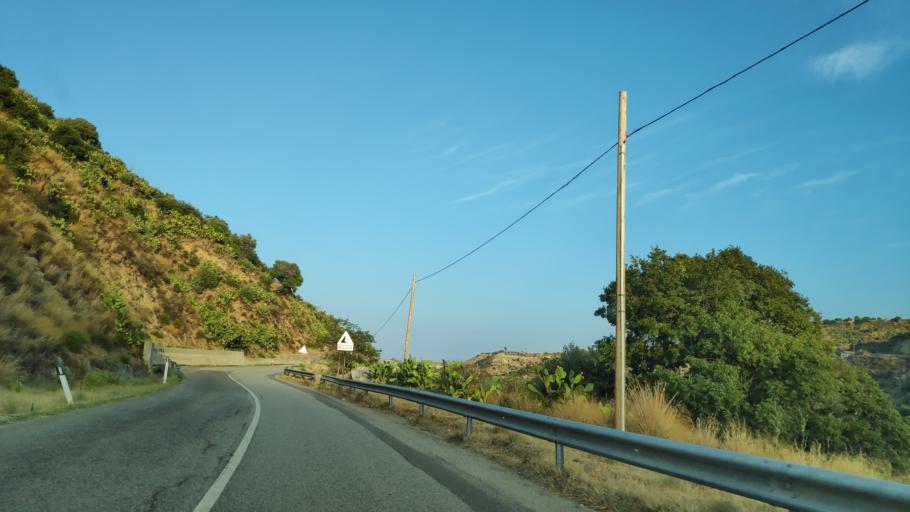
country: IT
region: Calabria
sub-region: Provincia di Catanzaro
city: Satriano
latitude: 38.6753
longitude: 16.4959
